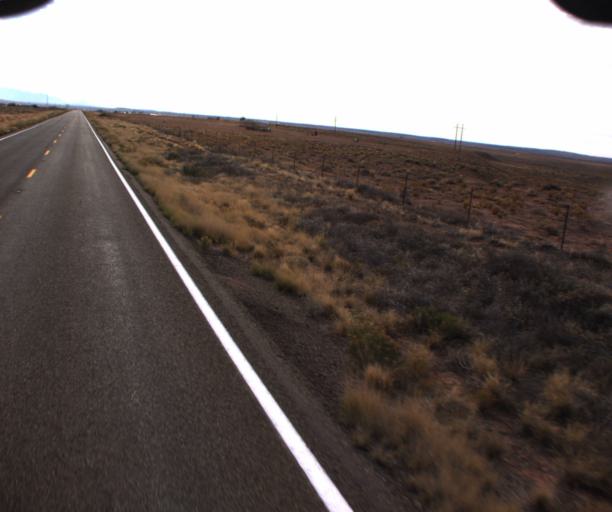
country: US
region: Arizona
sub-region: Apache County
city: Many Farms
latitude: 36.5211
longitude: -109.4919
